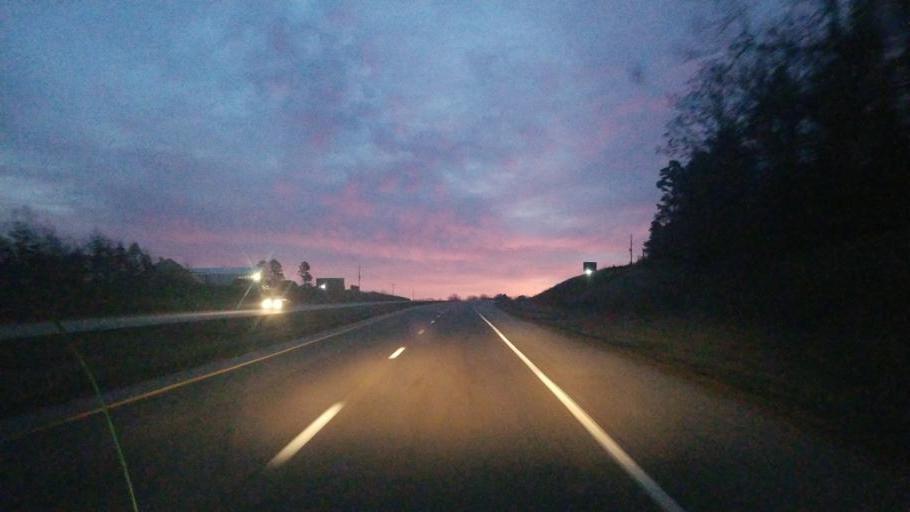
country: US
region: Missouri
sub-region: Shannon County
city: Winona
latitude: 36.9991
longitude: -91.4716
